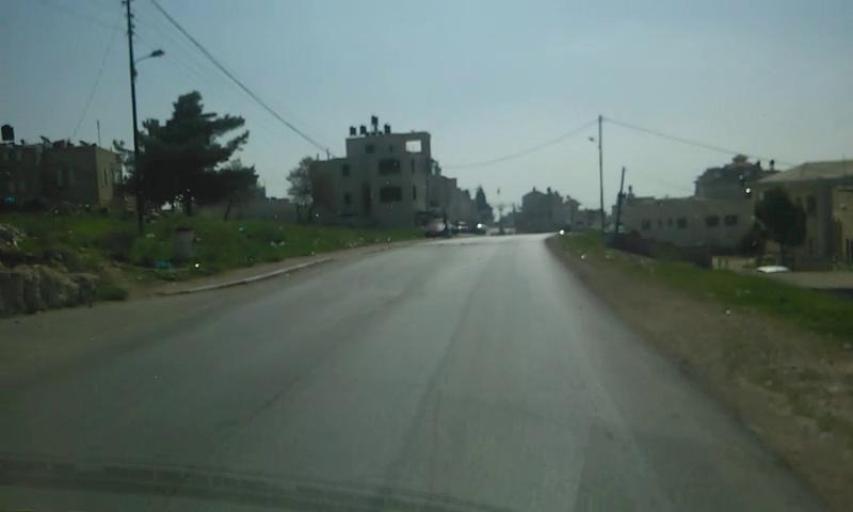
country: PS
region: West Bank
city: Dayr Jarir
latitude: 31.9665
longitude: 35.2919
